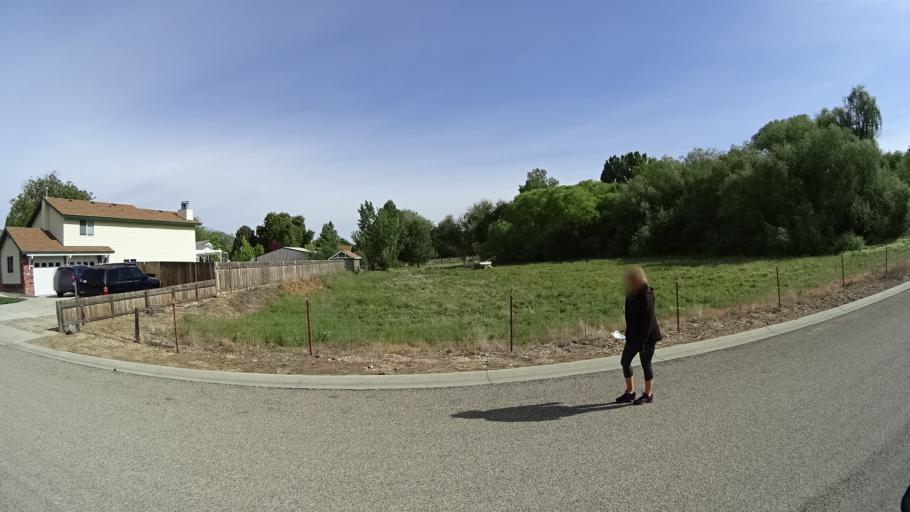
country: US
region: Idaho
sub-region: Ada County
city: Meridian
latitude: 43.5657
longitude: -116.3243
